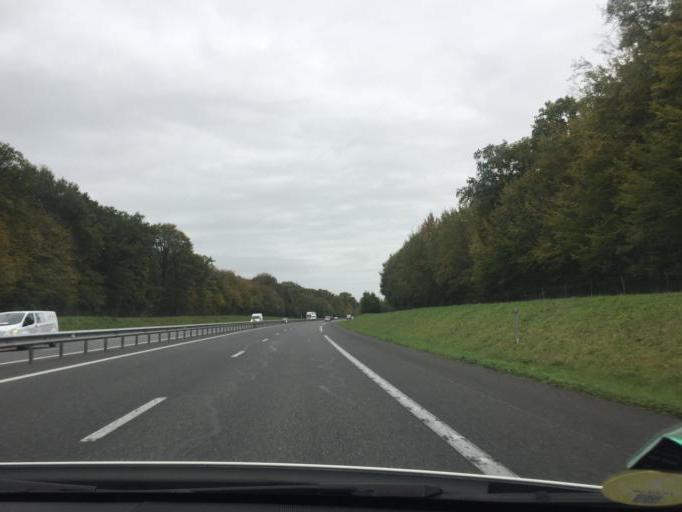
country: FR
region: Bourgogne
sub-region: Departement de l'Yonne
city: Egriselles-le-Bocage
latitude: 48.1101
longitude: 3.1344
